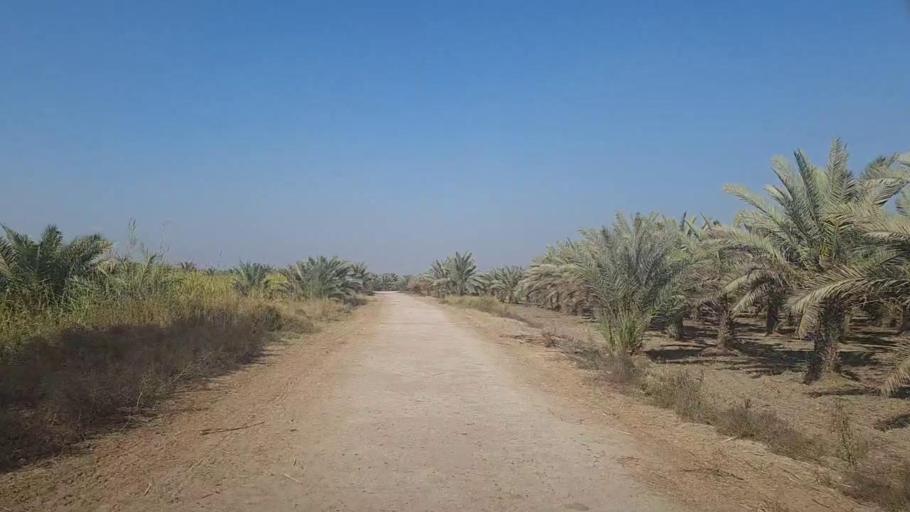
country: PK
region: Sindh
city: Kot Diji
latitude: 27.4332
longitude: 68.7376
